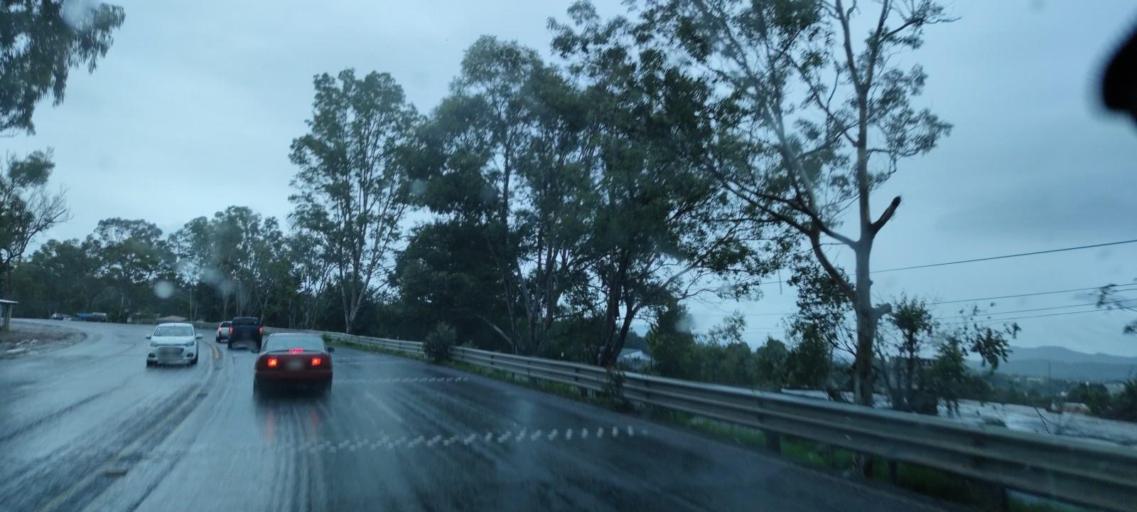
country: MX
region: Mexico
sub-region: Jilotepec
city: Doxhicho
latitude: 19.9349
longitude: -99.5674
